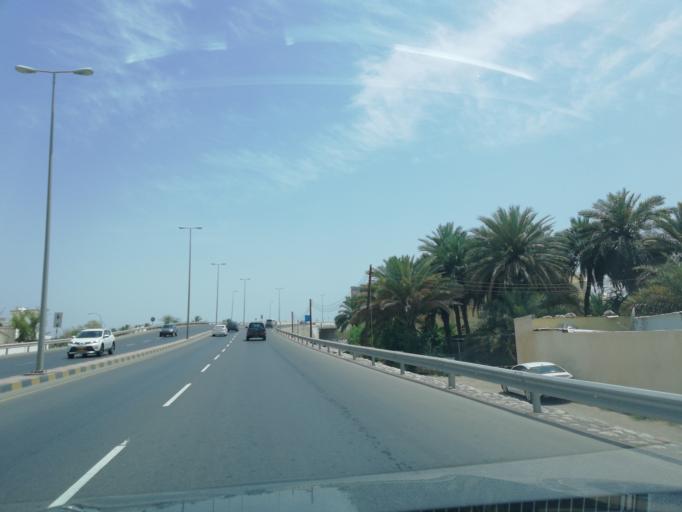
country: OM
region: Muhafazat Masqat
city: As Sib al Jadidah
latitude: 23.6777
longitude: 58.1384
